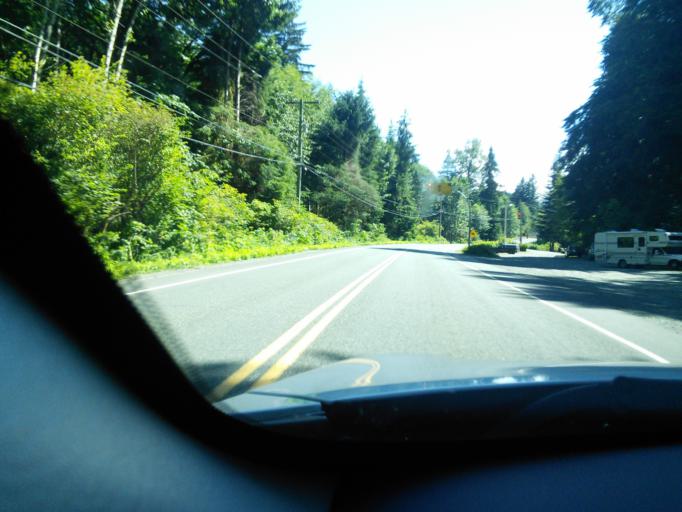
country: CA
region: British Columbia
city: Campbell River
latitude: 50.3227
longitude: -125.9221
